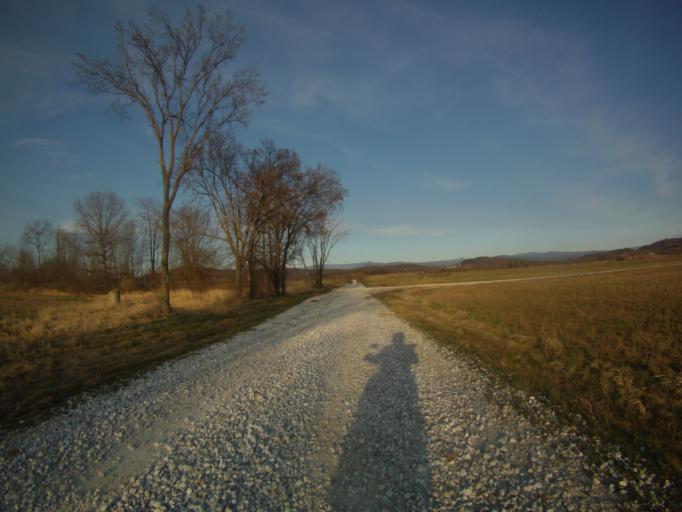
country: US
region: Vermont
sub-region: Addison County
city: Vergennes
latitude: 44.1000
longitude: -73.2851
